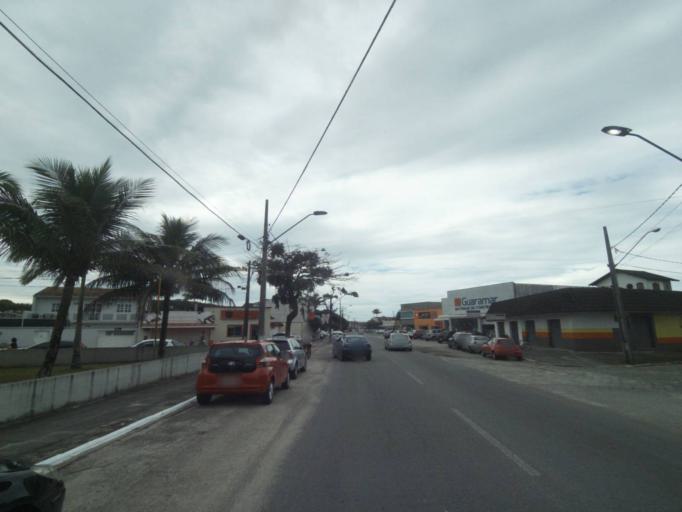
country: BR
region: Parana
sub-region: Guaratuba
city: Guaratuba
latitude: -25.8212
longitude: -48.5400
